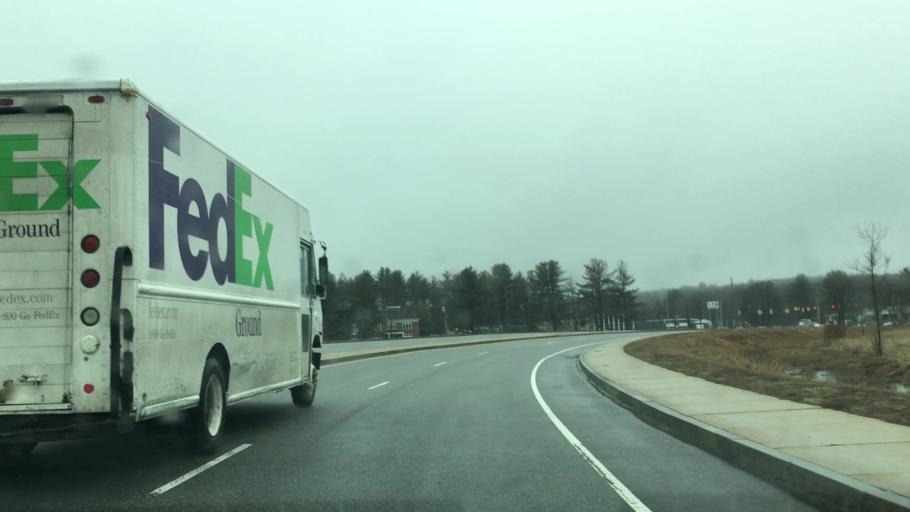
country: US
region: Massachusetts
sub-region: Middlesex County
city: Pinehurst
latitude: 42.5039
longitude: -71.2321
